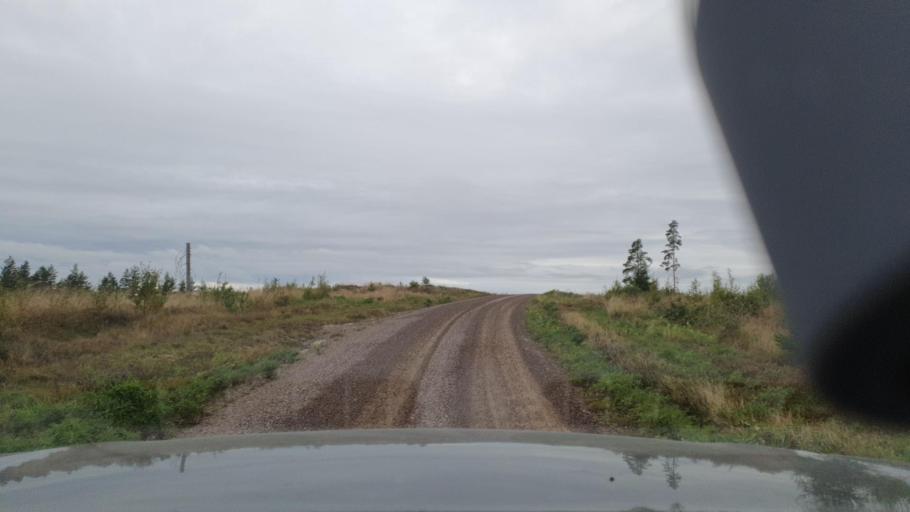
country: SE
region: Vaermland
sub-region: Torsby Kommun
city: Torsby
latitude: 59.9543
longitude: 12.7752
